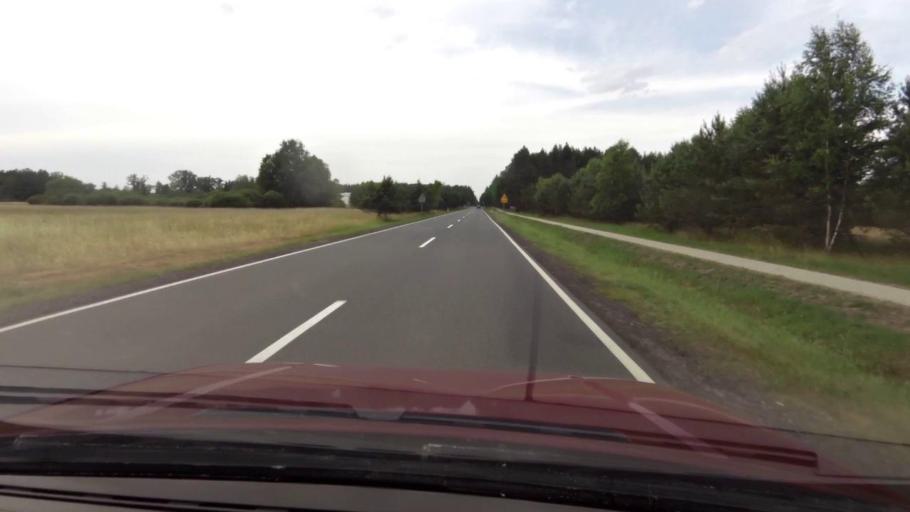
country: PL
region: Pomeranian Voivodeship
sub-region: Powiat bytowski
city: Trzebielino
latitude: 54.2137
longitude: 17.0892
